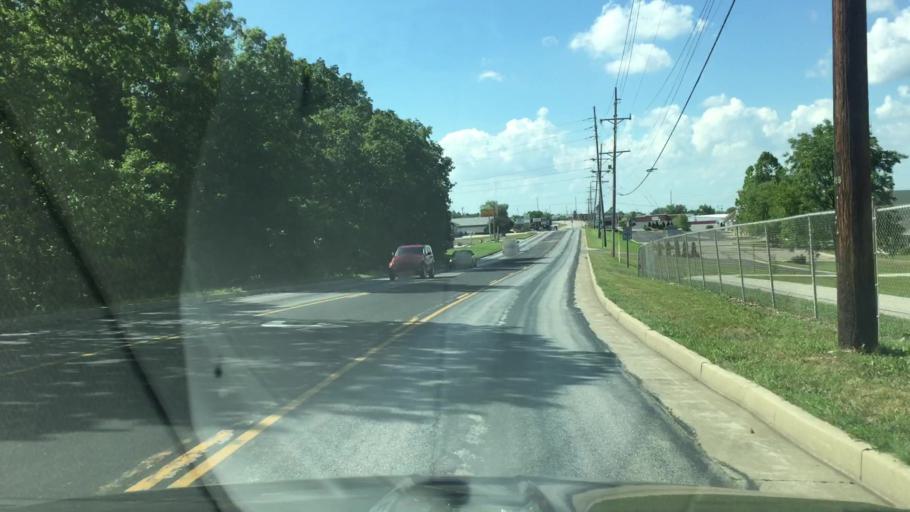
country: US
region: Missouri
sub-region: Camden County
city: Osage Beach
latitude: 38.1502
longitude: -92.5996
